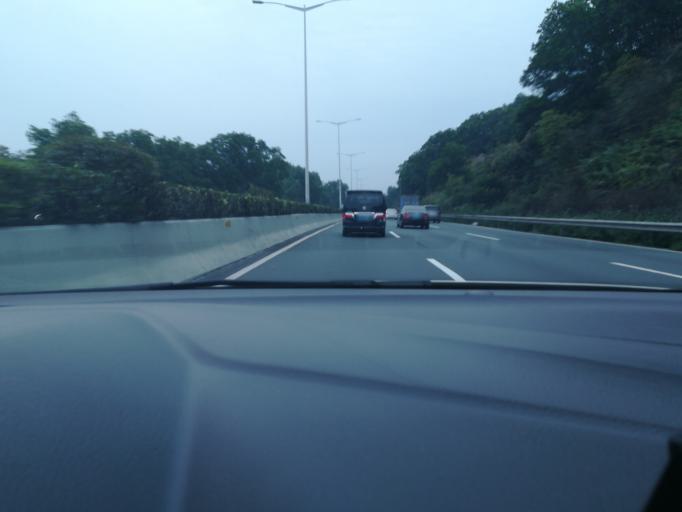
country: CN
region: Guangdong
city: Taihe
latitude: 23.2660
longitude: 113.3603
